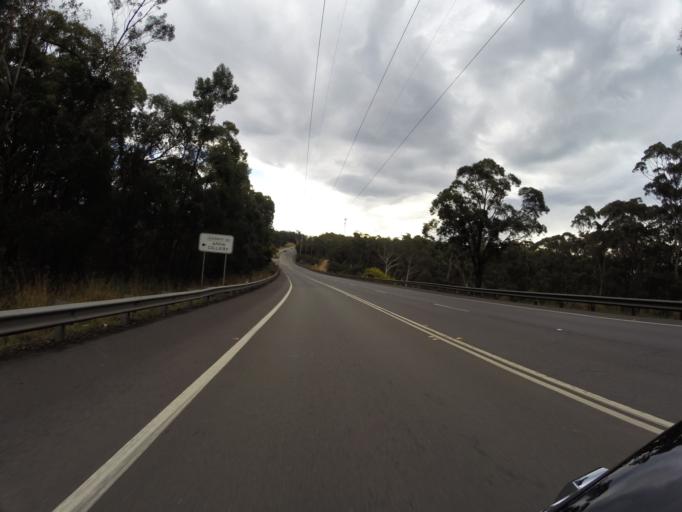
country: AU
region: New South Wales
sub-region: Wollondilly
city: Douglas Park
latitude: -34.2106
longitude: 150.7978
